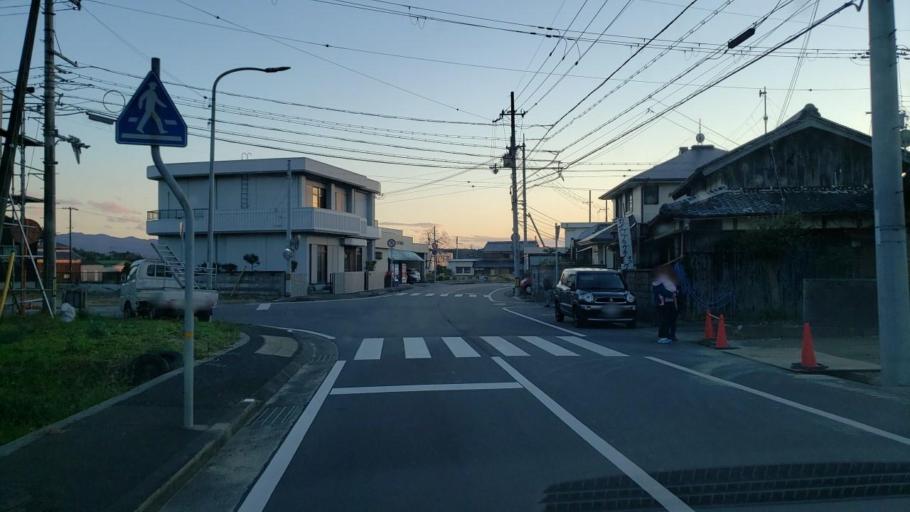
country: JP
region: Hyogo
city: Fukura
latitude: 34.3359
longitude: 134.7793
